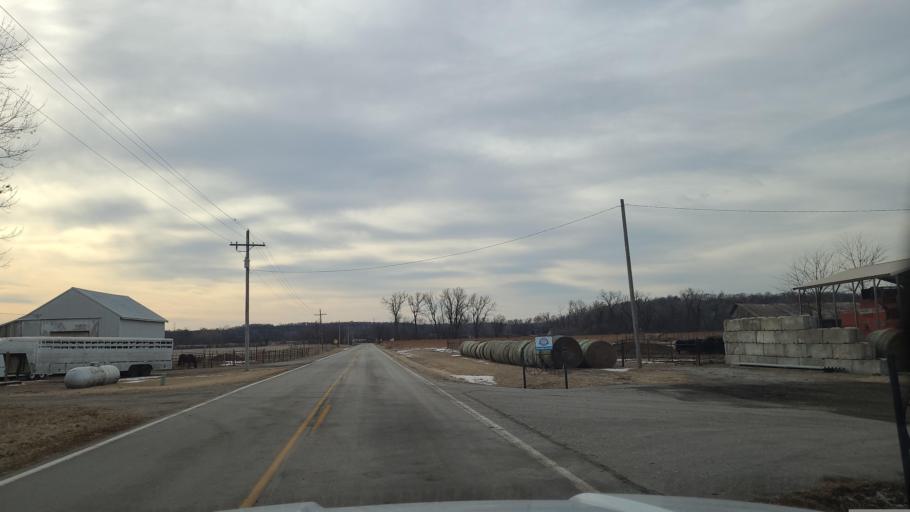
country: US
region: Kansas
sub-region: Douglas County
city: Lawrence
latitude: 39.0175
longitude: -95.2935
